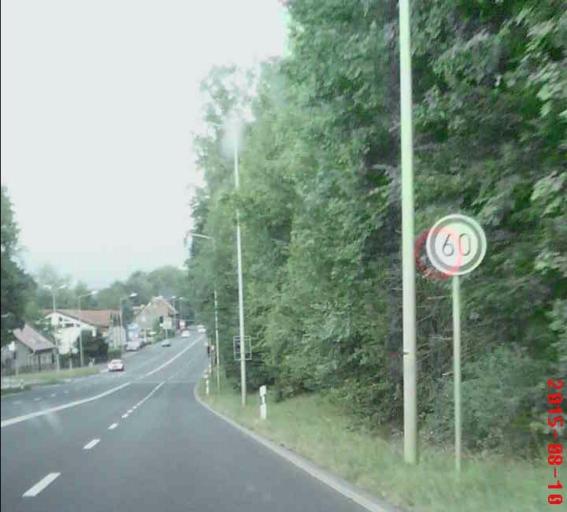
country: DE
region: Thuringia
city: Suhl
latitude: 50.5983
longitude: 10.6584
